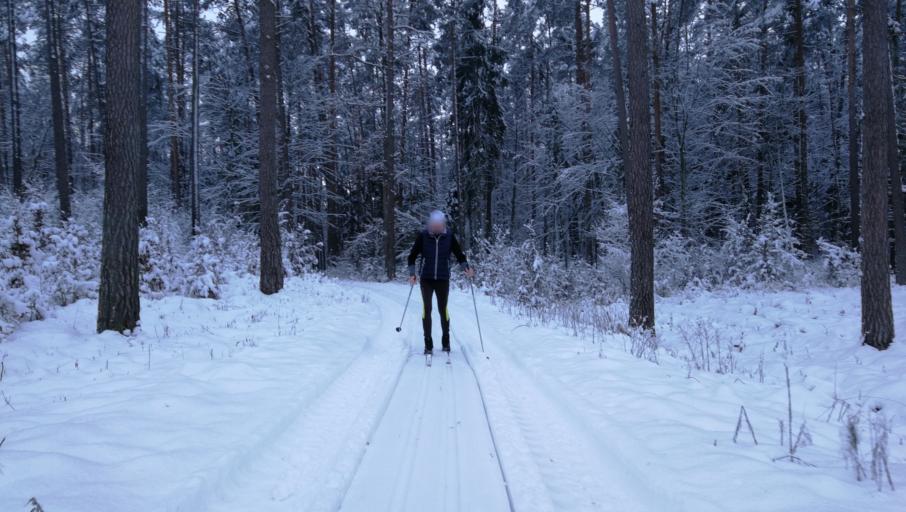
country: PL
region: Kujawsko-Pomorskie
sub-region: Powiat brodnicki
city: Gorzno
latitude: 53.2072
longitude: 19.6968
